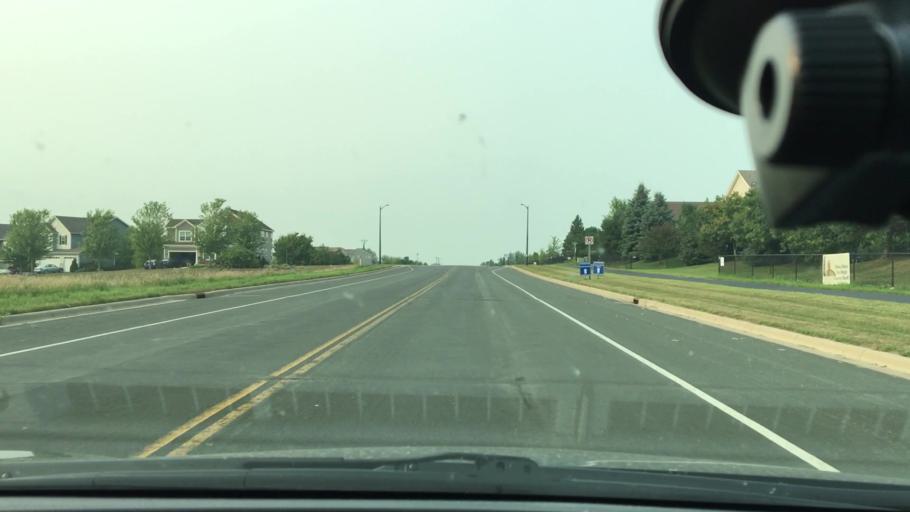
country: US
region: Minnesota
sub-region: Wright County
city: Albertville
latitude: 45.2478
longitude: -93.6428
